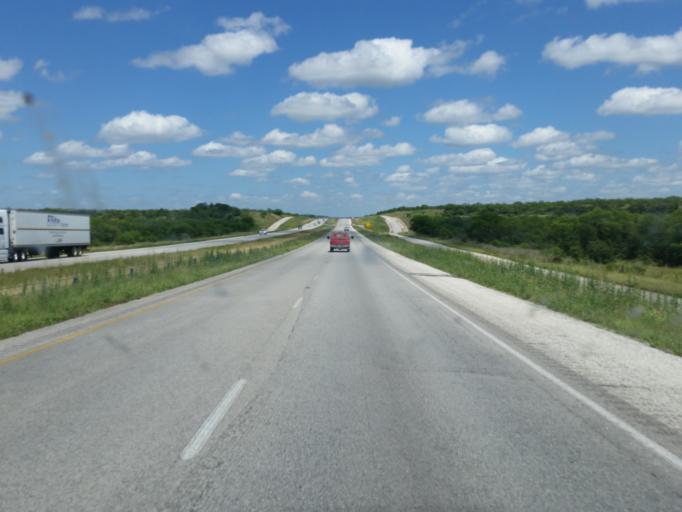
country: US
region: Texas
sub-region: Callahan County
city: Baird
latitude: 32.3820
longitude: -99.2757
